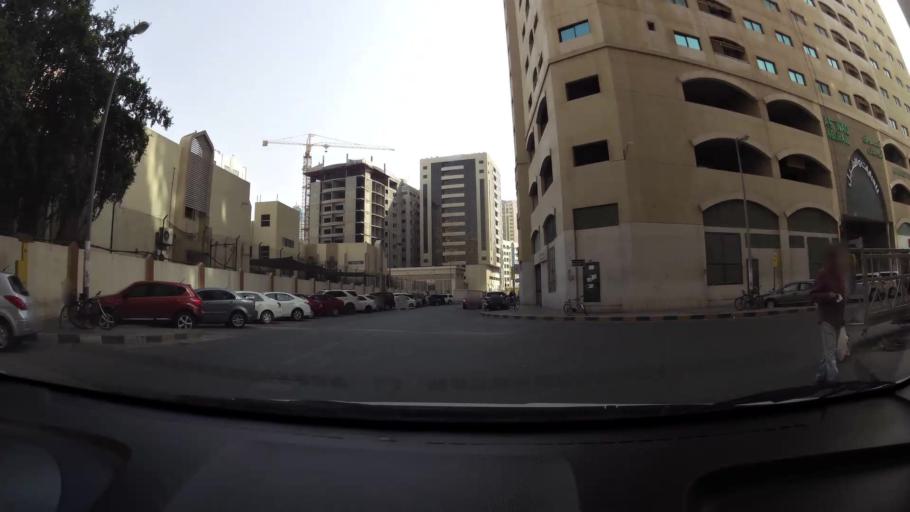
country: AE
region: Ash Shariqah
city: Sharjah
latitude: 25.3400
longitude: 55.3914
